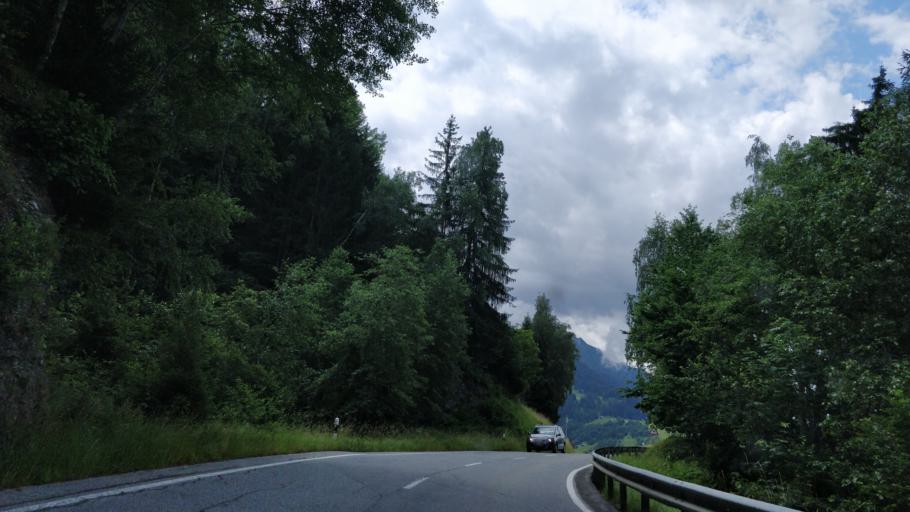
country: CH
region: Grisons
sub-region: Surselva District
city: Ilanz
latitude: 46.7083
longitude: 9.1933
